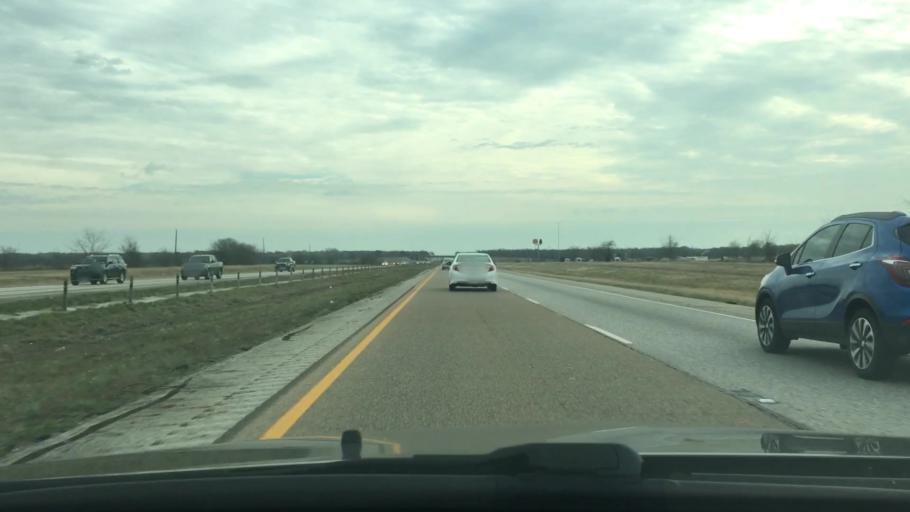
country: US
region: Texas
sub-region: Leon County
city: Centerville
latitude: 31.1014
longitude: -95.9641
